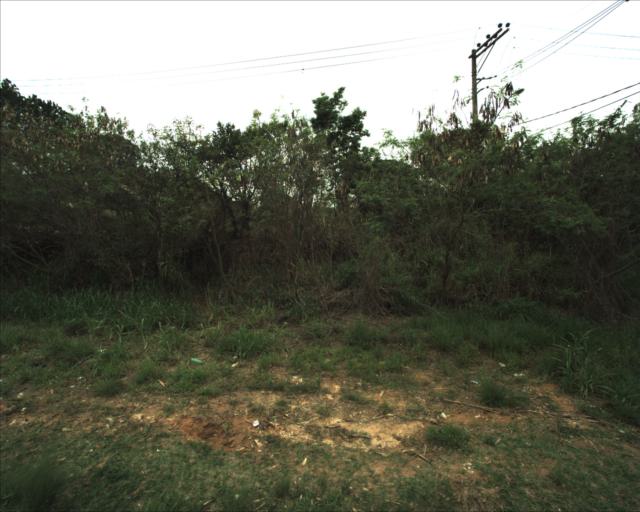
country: BR
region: Sao Paulo
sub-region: Sorocaba
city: Sorocaba
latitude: -23.4516
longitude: -47.3791
